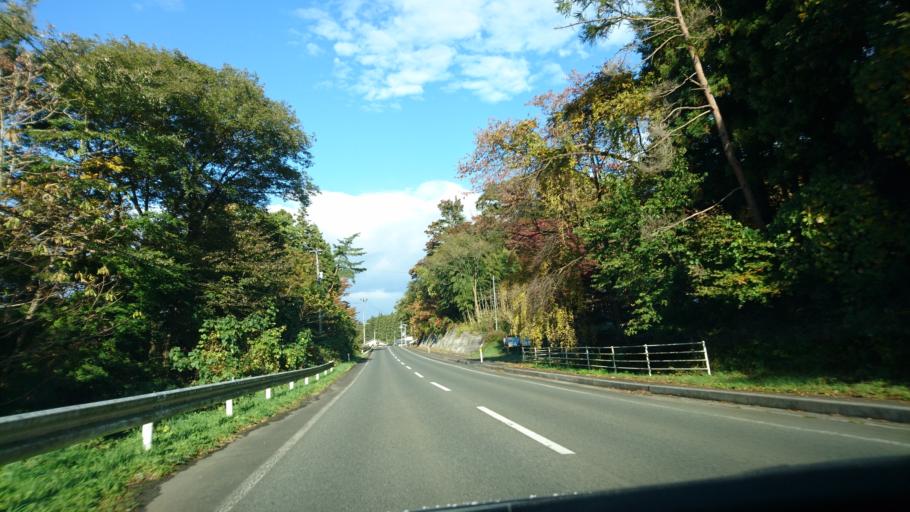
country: JP
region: Iwate
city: Mizusawa
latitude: 39.0365
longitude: 141.0716
